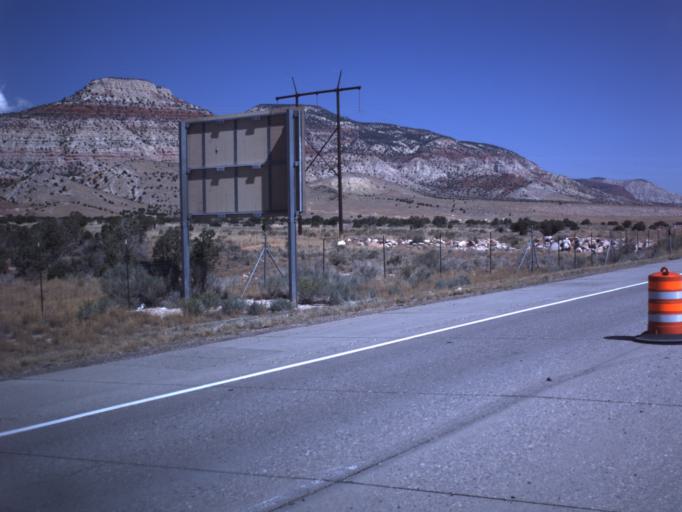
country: US
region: Utah
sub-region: Sevier County
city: Richfield
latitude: 38.8089
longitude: -112.0594
